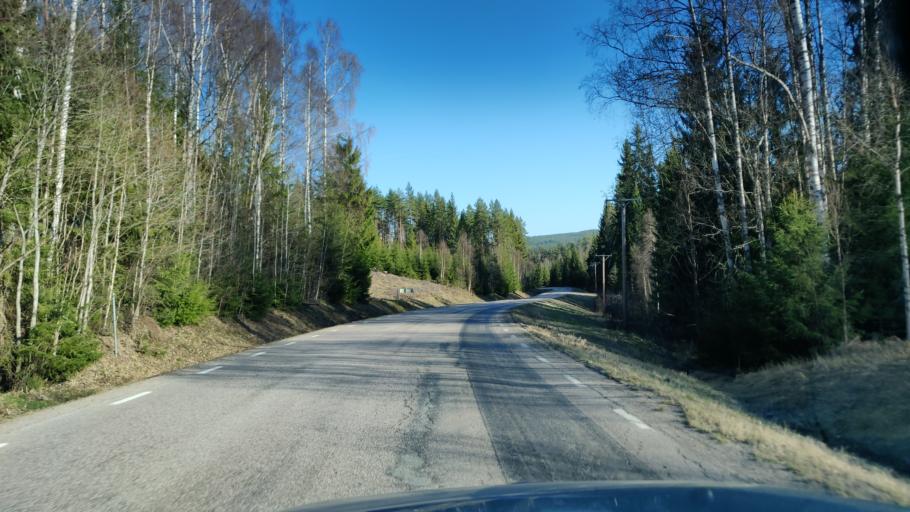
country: SE
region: Vaermland
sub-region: Munkfors Kommun
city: Munkfors
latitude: 59.9833
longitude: 13.4026
